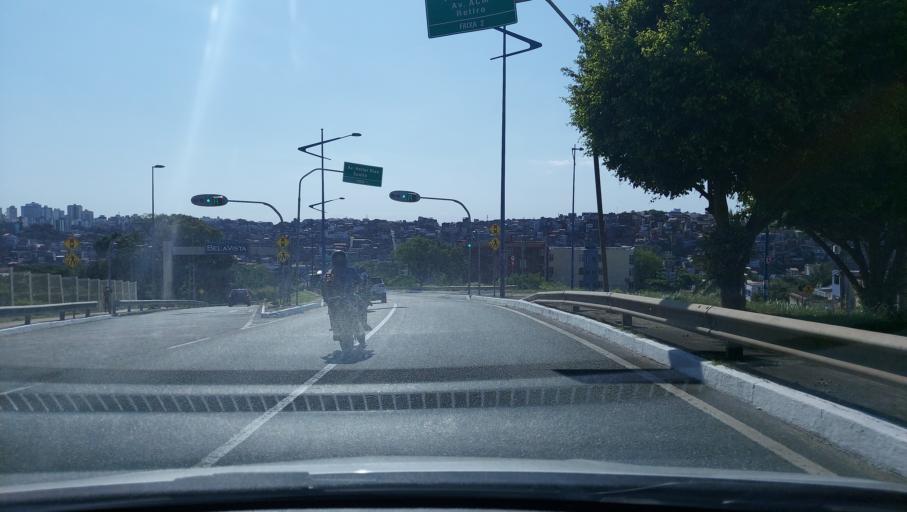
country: BR
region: Bahia
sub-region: Salvador
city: Salvador
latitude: -12.9653
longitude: -38.4743
